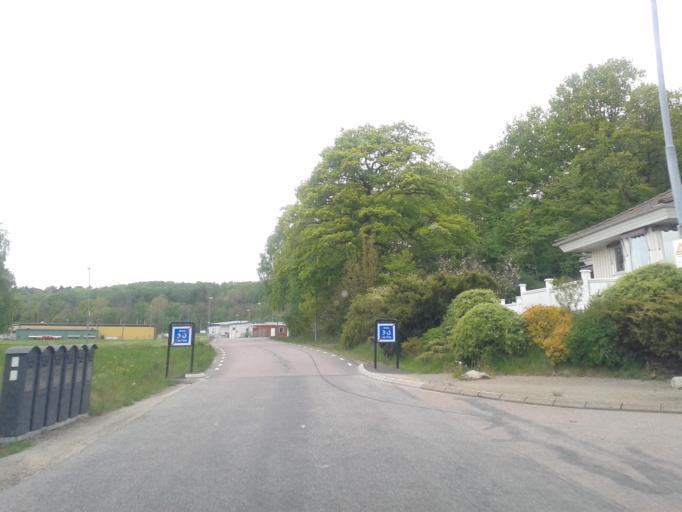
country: SE
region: Vaestra Goetaland
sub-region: Kungalvs Kommun
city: Kungalv
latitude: 57.8845
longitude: 11.9928
